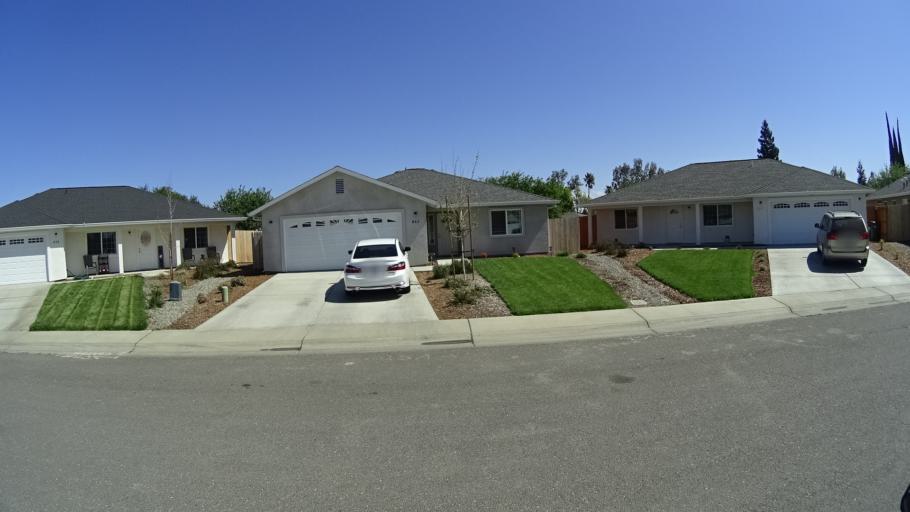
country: US
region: California
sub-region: Glenn County
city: Orland
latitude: 39.7452
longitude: -122.2043
